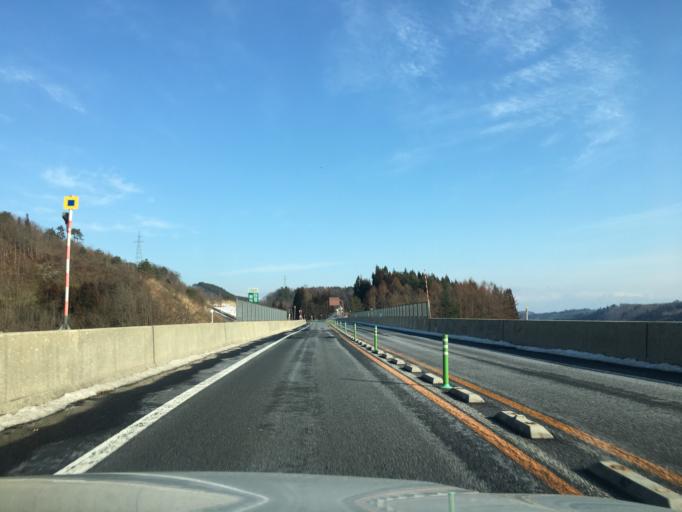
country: JP
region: Yamagata
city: Sagae
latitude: 38.4377
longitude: 140.1287
